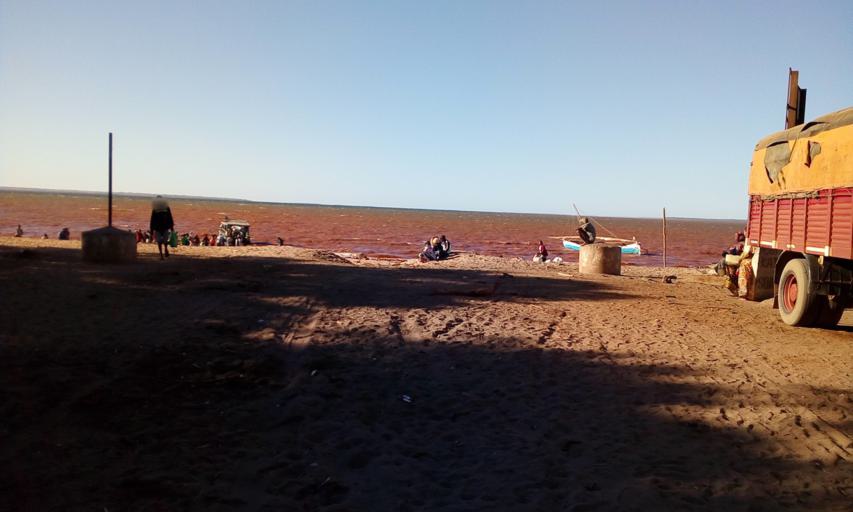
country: MG
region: Boeny
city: Mahajanga
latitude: -15.7660
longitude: 46.2422
